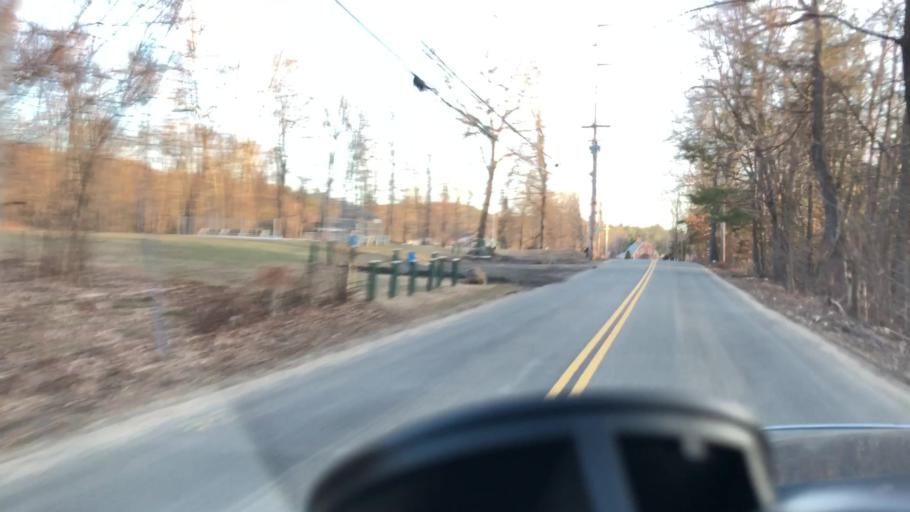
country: US
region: Massachusetts
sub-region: Hampshire County
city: Southampton
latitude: 42.2010
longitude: -72.6796
